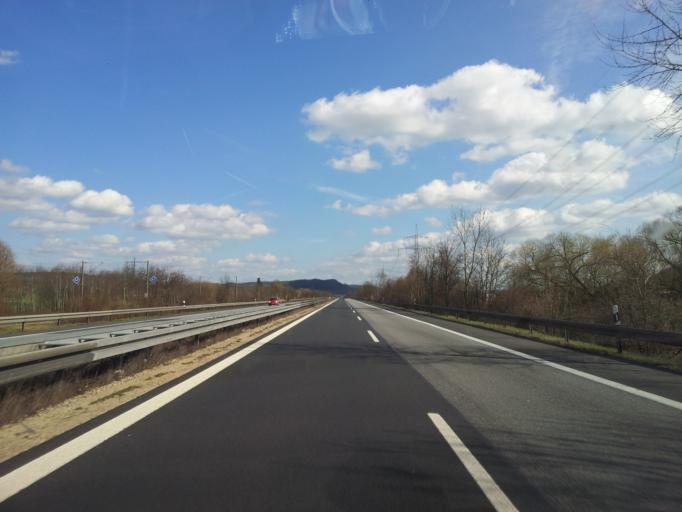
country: DE
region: Bavaria
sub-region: Regierungsbezirk Unterfranken
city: Ebelsbach
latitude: 49.9745
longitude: 10.6943
